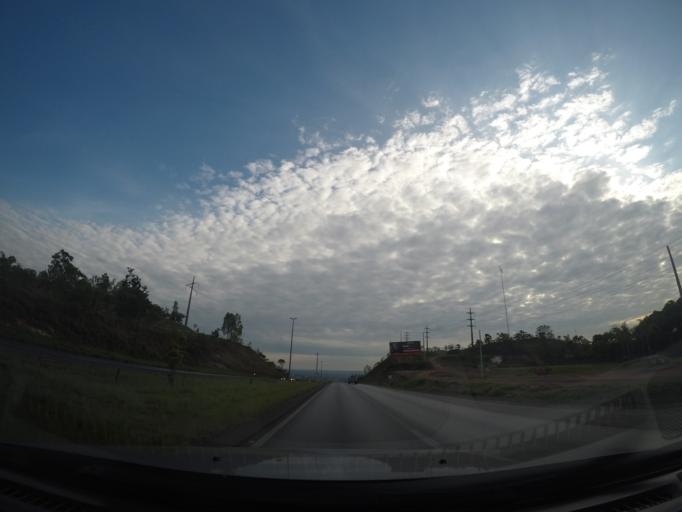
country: BR
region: Goias
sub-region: Planaltina
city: Planaltina
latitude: -15.6199
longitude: -47.7143
